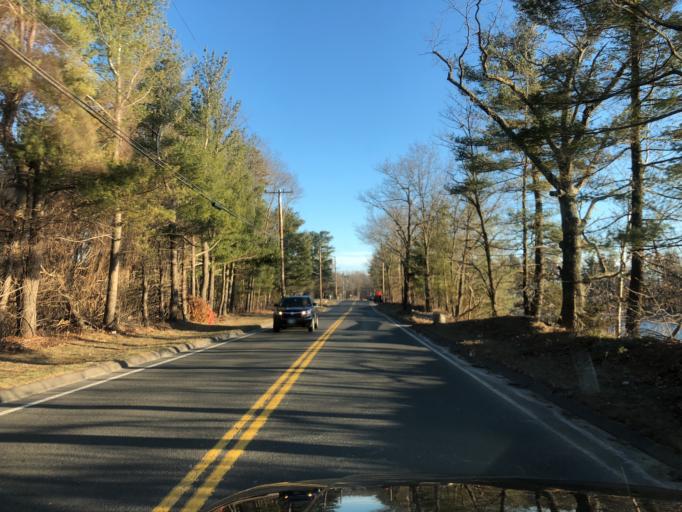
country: US
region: Connecticut
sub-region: Hartford County
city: Farmington
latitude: 41.7437
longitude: -72.8531
